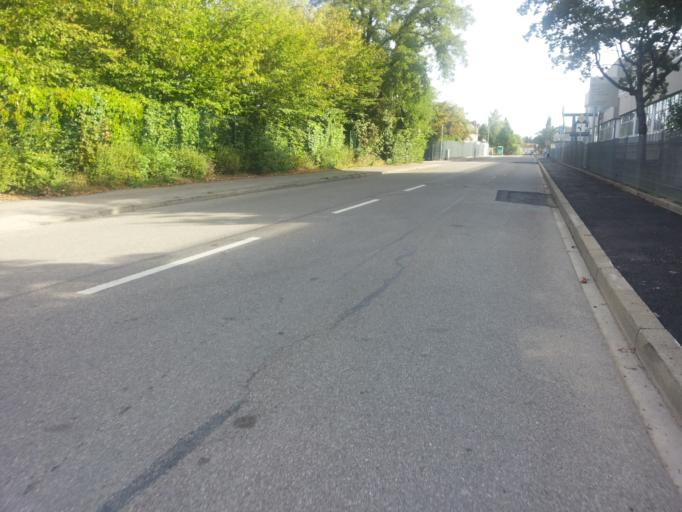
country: DE
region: Bavaria
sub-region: Upper Bavaria
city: Ingolstadt
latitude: 48.7799
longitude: 11.4202
